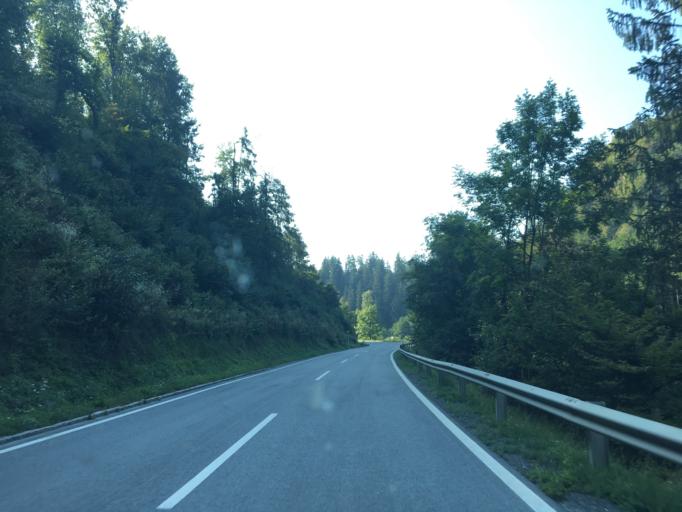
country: AT
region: Carinthia
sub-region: Politischer Bezirk Volkermarkt
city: Diex
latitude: 46.7018
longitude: 14.5686
